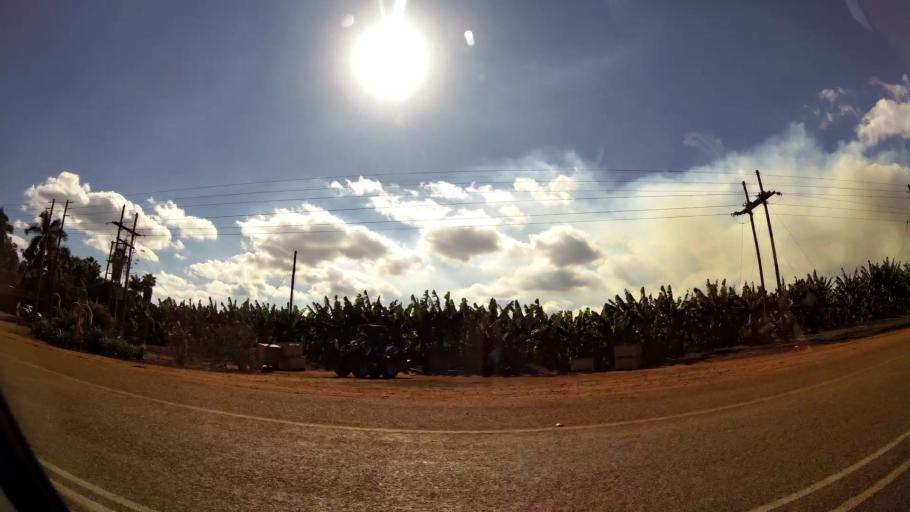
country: ZA
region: Limpopo
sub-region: Mopani District Municipality
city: Tzaneen
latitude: -23.8037
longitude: 30.1068
